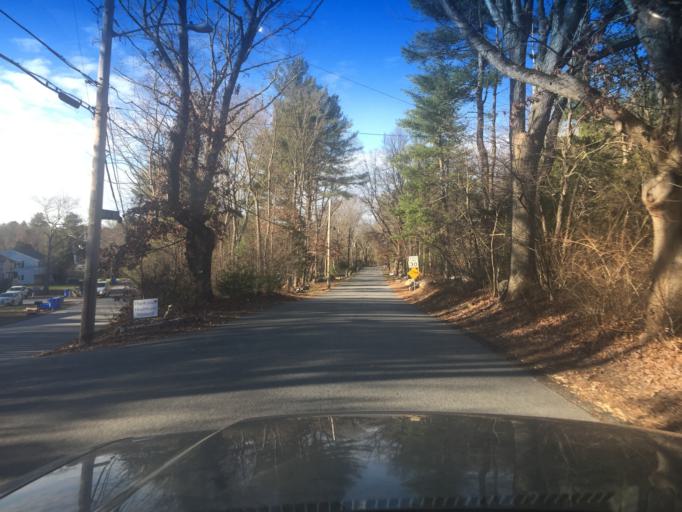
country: US
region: Massachusetts
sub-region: Middlesex County
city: Holliston
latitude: 42.2085
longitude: -71.4601
